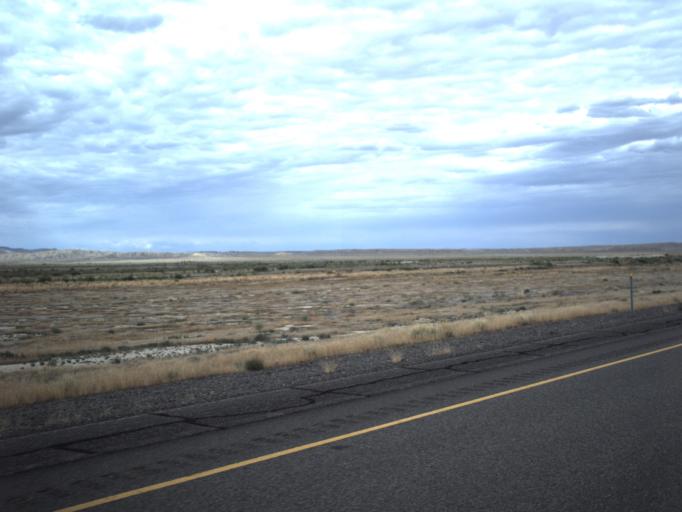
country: US
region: Utah
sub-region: Grand County
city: Moab
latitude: 38.9418
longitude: -109.5823
